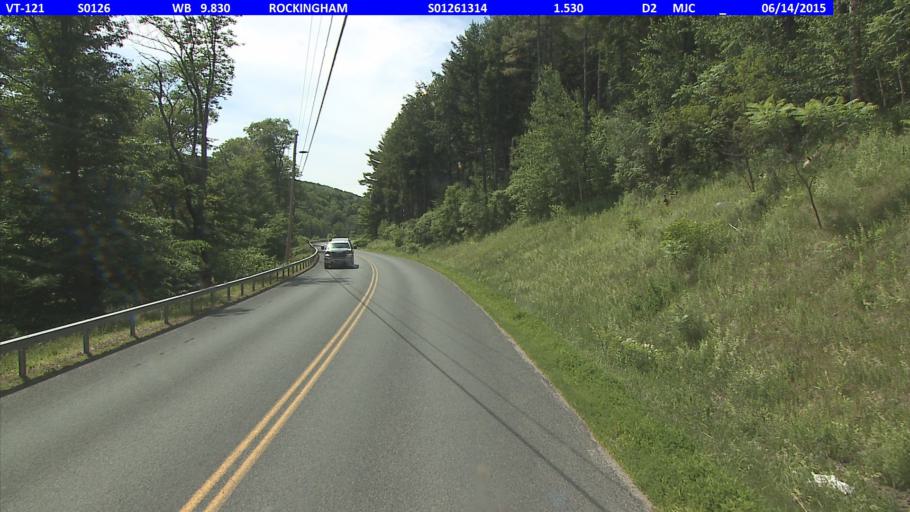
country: US
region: Vermont
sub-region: Windham County
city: Rockingham
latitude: 43.1397
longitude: -72.5334
